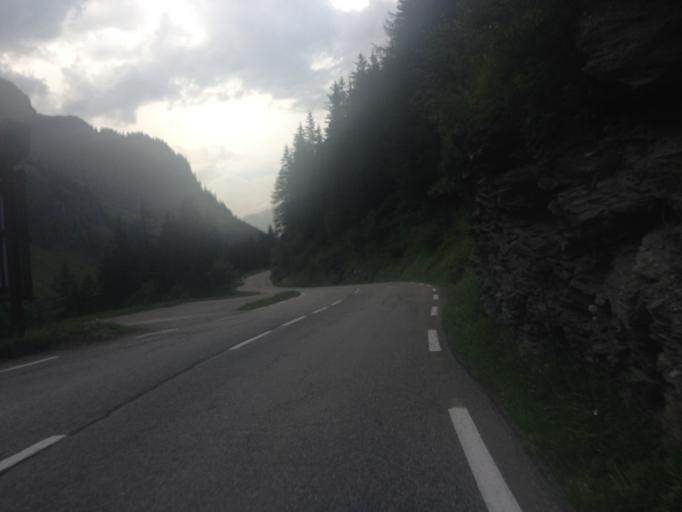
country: FR
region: Rhone-Alpes
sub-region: Departement de la Savoie
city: Tignes
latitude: 45.5224
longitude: 6.9138
